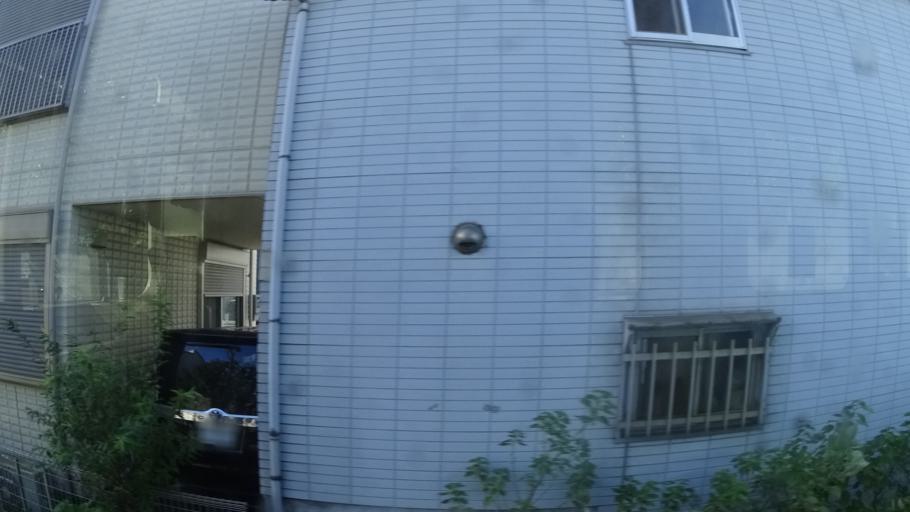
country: JP
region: Kanagawa
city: Kamakura
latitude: 35.3118
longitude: 139.5383
